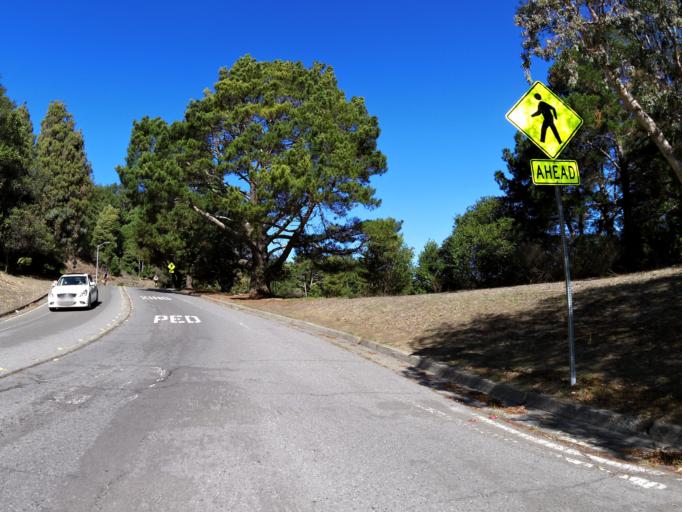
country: US
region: California
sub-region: Marin County
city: Mill Valley
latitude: 37.9079
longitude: -122.5280
